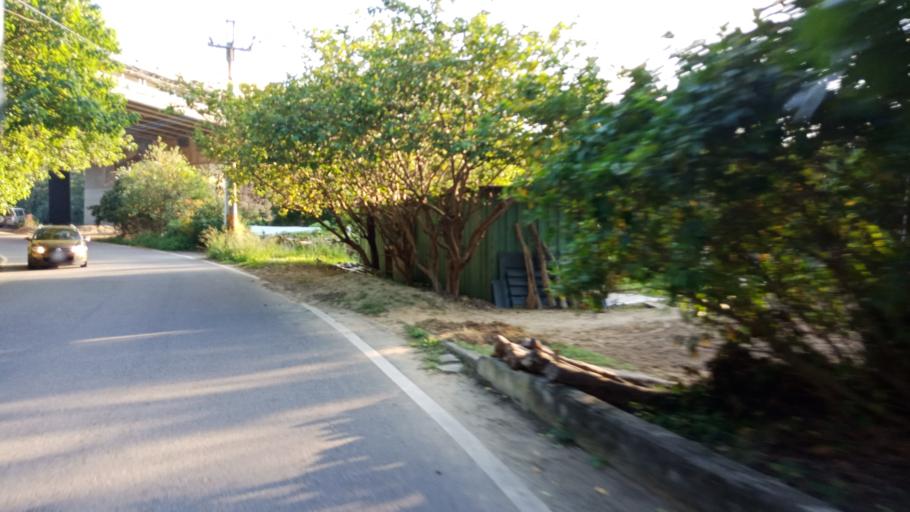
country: TW
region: Taiwan
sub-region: Hsinchu
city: Hsinchu
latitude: 24.7660
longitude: 121.0004
